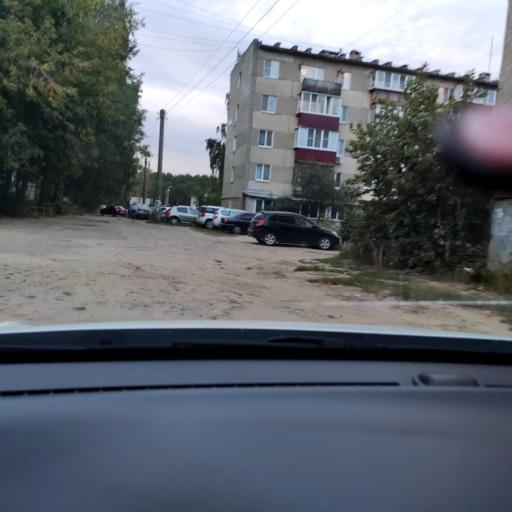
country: RU
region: Mariy-El
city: Volzhsk
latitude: 55.8659
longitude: 48.3463
